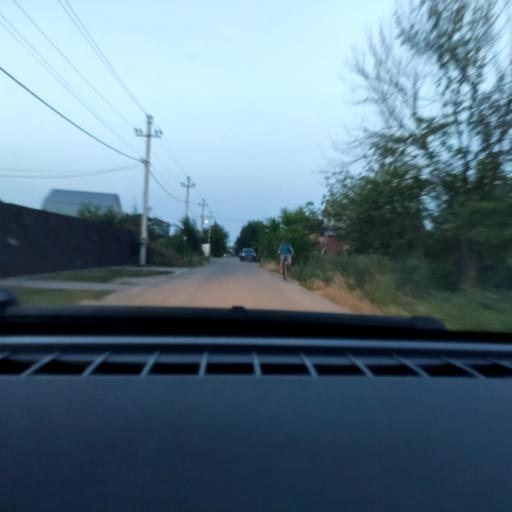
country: RU
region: Voronezj
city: Somovo
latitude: 51.6800
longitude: 39.3094
